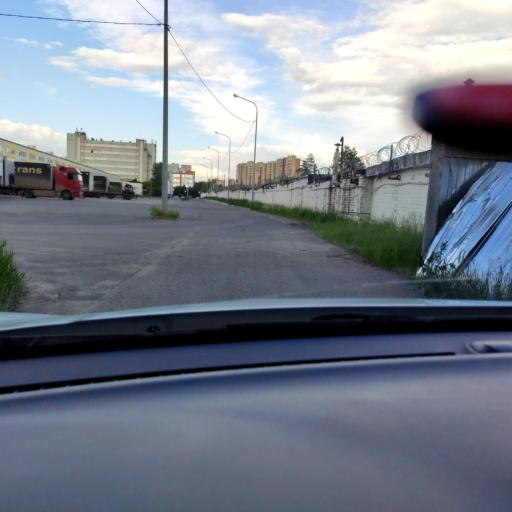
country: RU
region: Tatarstan
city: Staroye Arakchino
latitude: 55.8287
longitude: 49.0381
